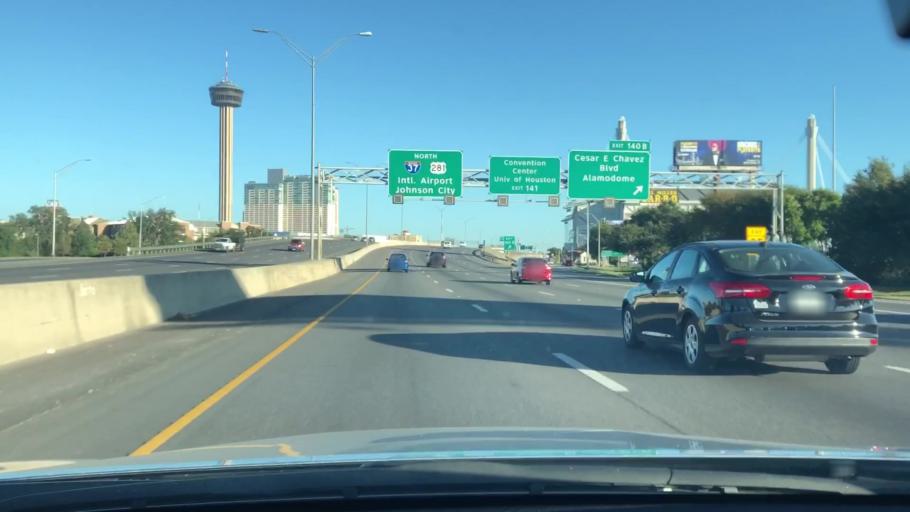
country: US
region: Texas
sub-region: Bexar County
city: San Antonio
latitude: 29.4112
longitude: -98.4799
